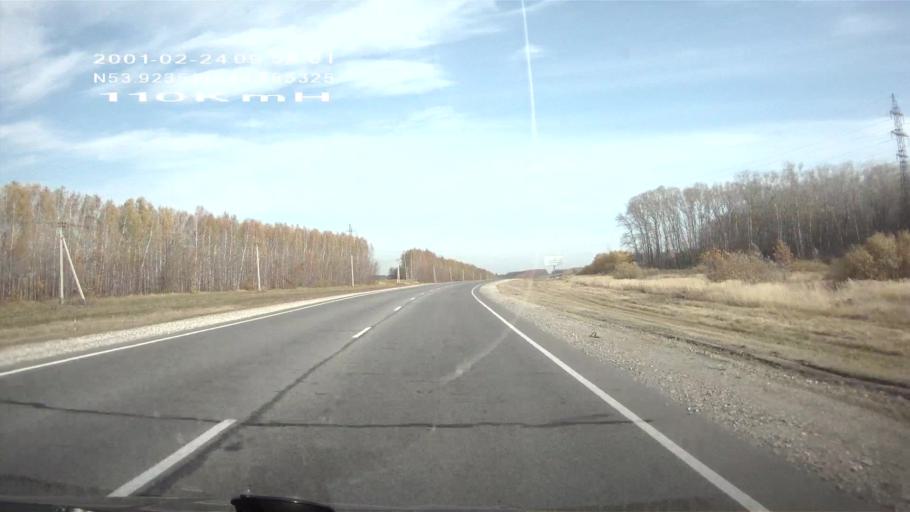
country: RU
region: Penza
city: Issa
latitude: 53.9240
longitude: 44.8655
